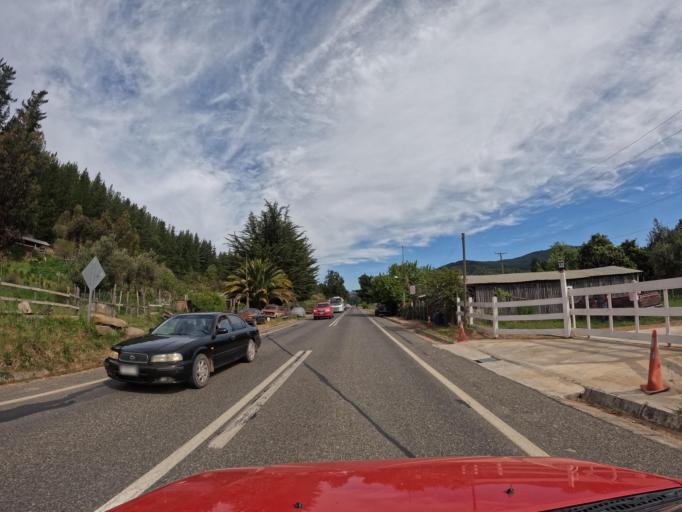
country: CL
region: Maule
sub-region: Provincia de Talca
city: Talca
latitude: -35.3094
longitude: -71.9637
